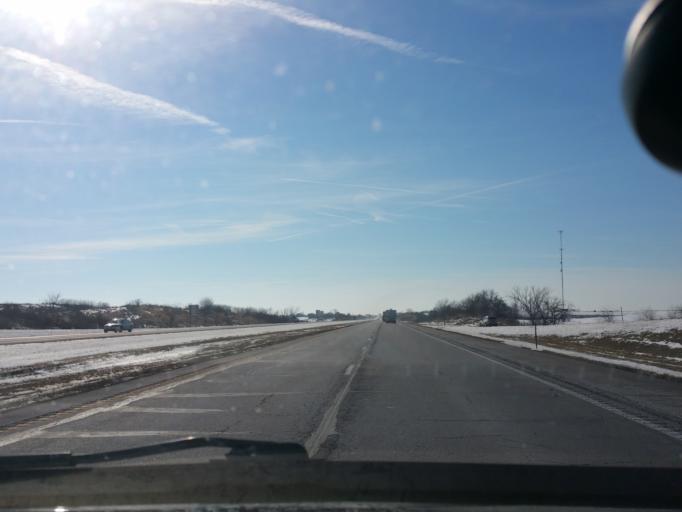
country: US
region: Missouri
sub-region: Harrison County
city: Bethany
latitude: 40.3731
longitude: -94.0035
